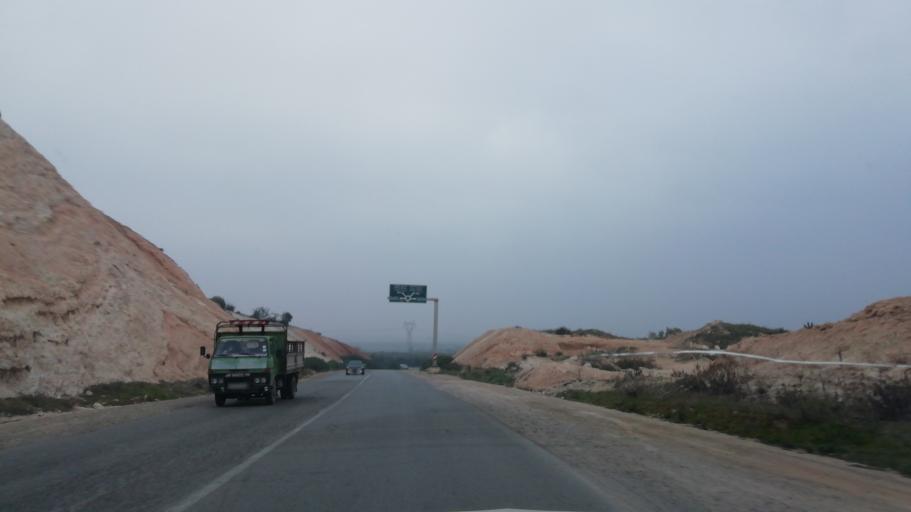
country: DZ
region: Mascara
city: Mascara
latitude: 35.3834
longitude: 0.1612
